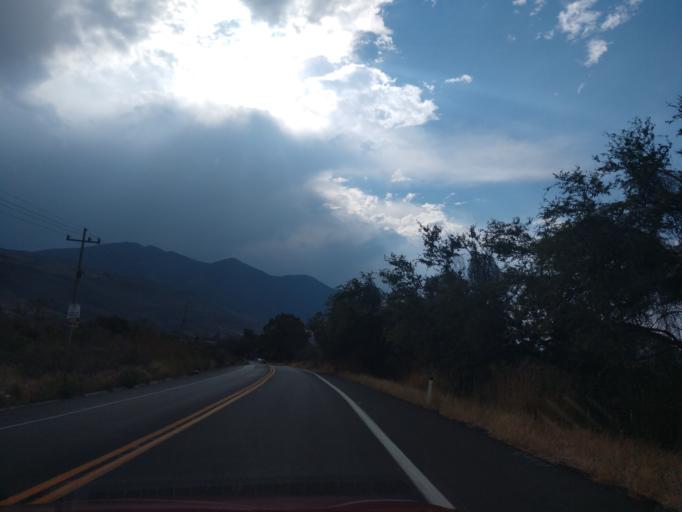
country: MX
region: Jalisco
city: San Juan Cosala
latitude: 20.1942
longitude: -103.2854
